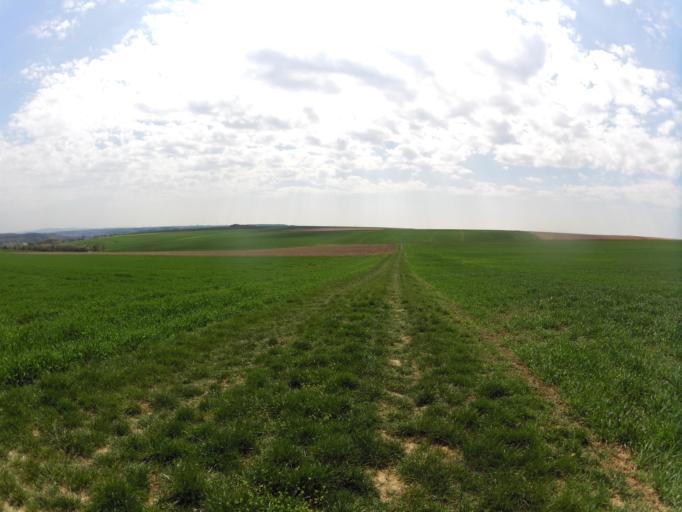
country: DE
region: Bavaria
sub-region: Regierungsbezirk Unterfranken
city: Winterhausen
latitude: 49.6885
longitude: 10.0055
